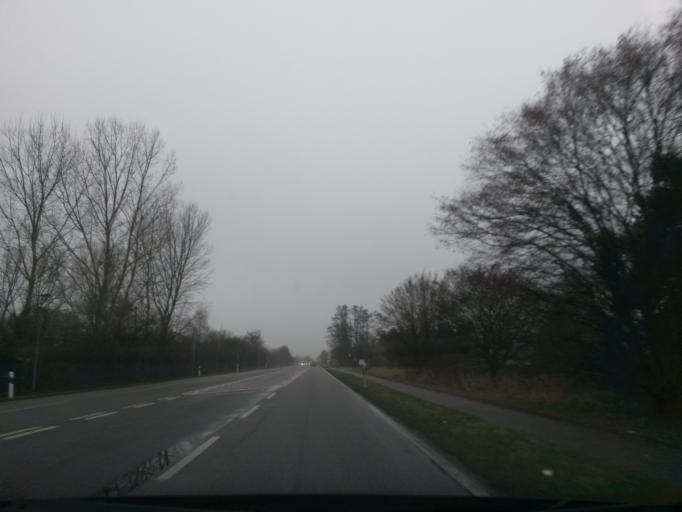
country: DE
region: Baden-Wuerttemberg
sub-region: Karlsruhe Region
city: Karlsruhe
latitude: 49.0385
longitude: 8.3942
